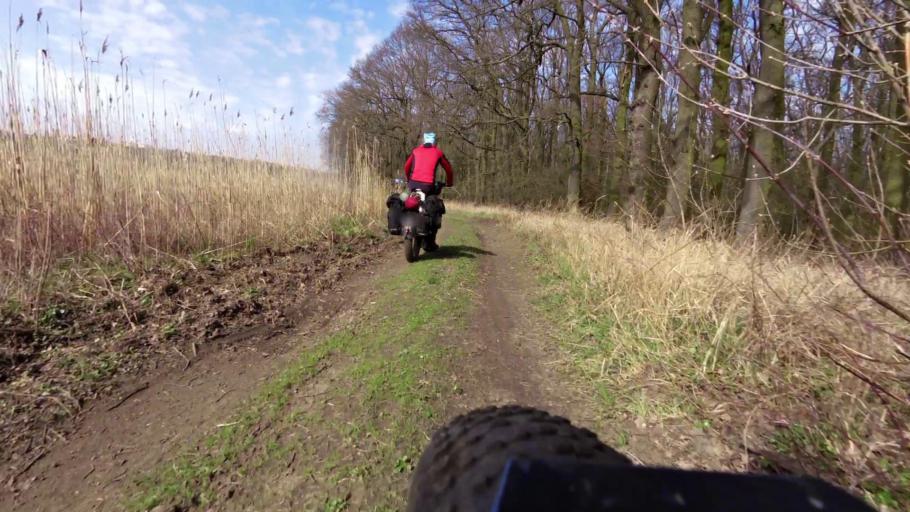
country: PL
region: Lubusz
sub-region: Powiat slubicki
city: Slubice
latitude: 52.3266
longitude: 14.5697
